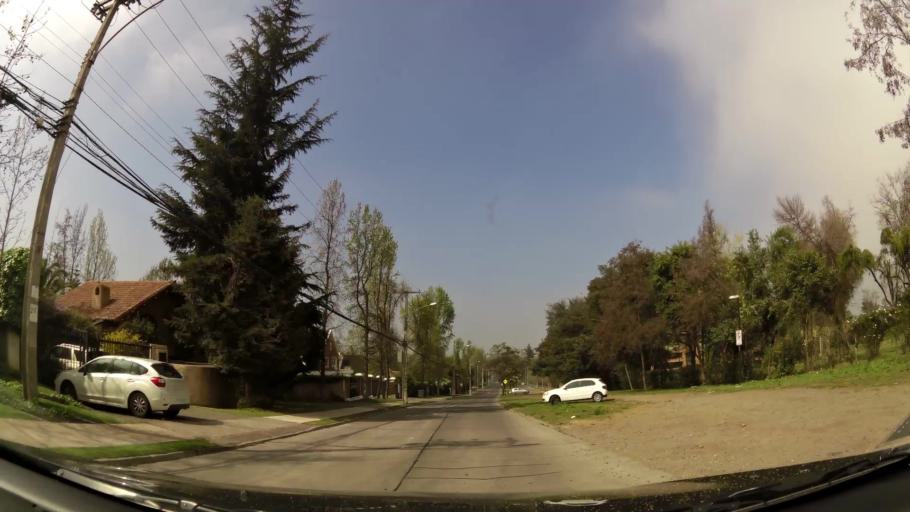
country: CL
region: Santiago Metropolitan
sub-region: Provincia de Santiago
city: Villa Presidente Frei, Nunoa, Santiago, Chile
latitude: -33.3729
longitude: -70.5841
